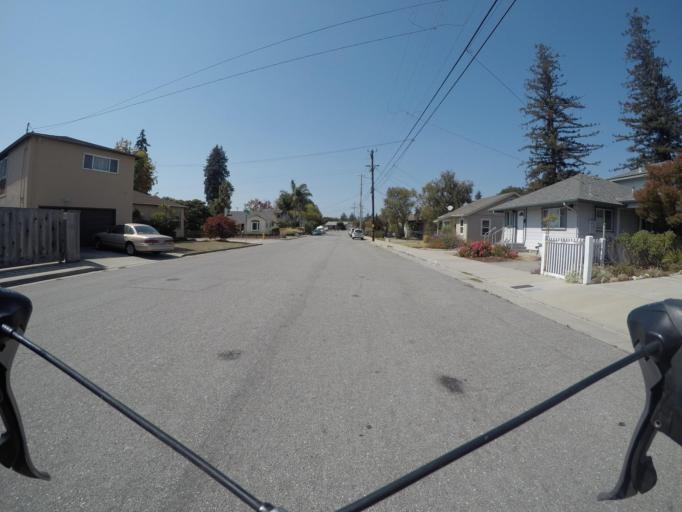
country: US
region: California
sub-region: Santa Cruz County
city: Twin Lakes
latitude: 36.9863
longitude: -122.0102
